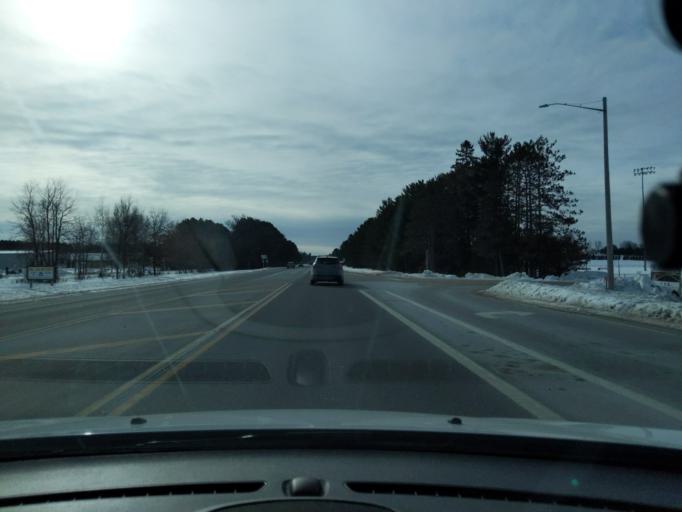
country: US
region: Wisconsin
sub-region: Washburn County
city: Shell Lake
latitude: 45.7302
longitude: -91.9316
